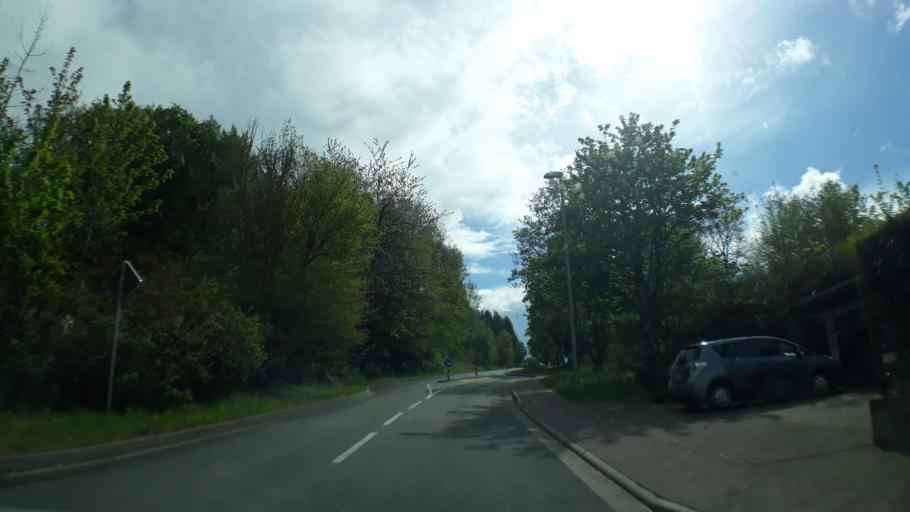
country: DE
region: North Rhine-Westphalia
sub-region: Regierungsbezirk Koln
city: Kall
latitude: 50.5117
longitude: 6.5422
